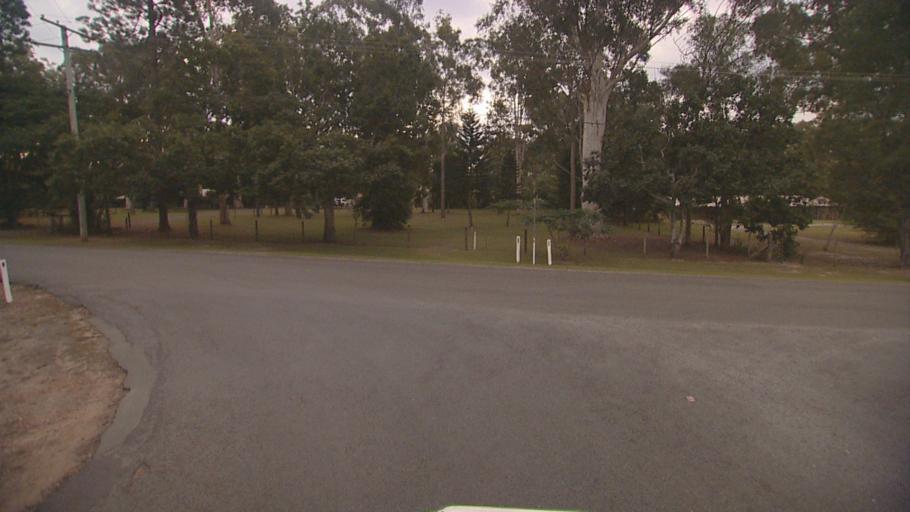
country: AU
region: Queensland
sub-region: Logan
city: Chambers Flat
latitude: -27.7877
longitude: 153.1122
